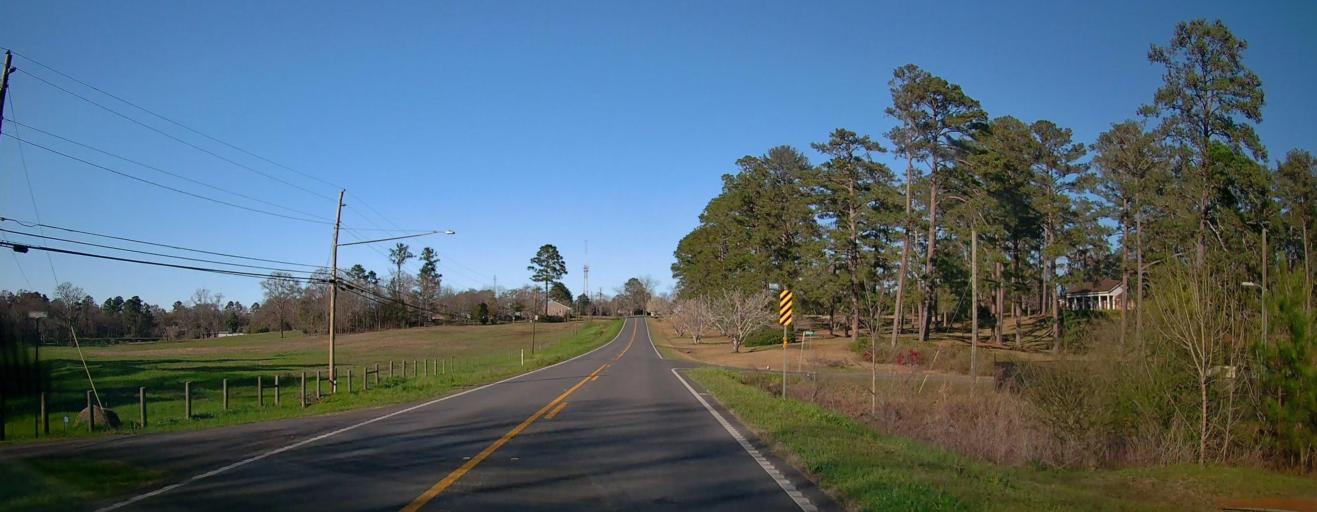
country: US
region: Georgia
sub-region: Taylor County
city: Reynolds
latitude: 32.5511
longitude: -84.0979
